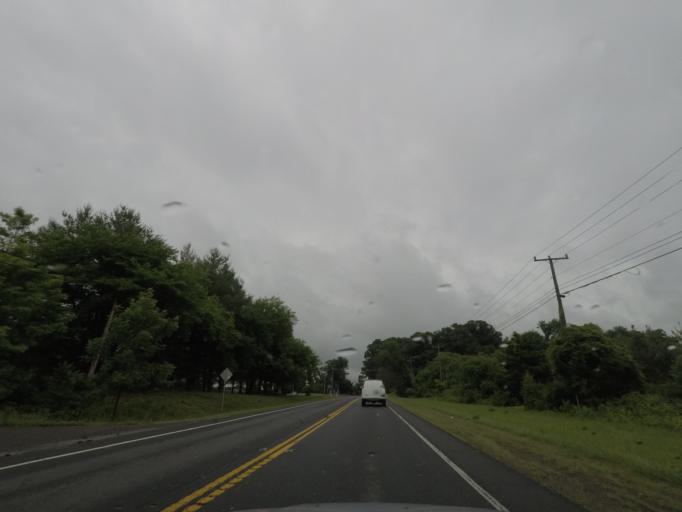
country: US
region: Virginia
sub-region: Loudoun County
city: Leesburg
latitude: 39.0803
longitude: -77.6038
